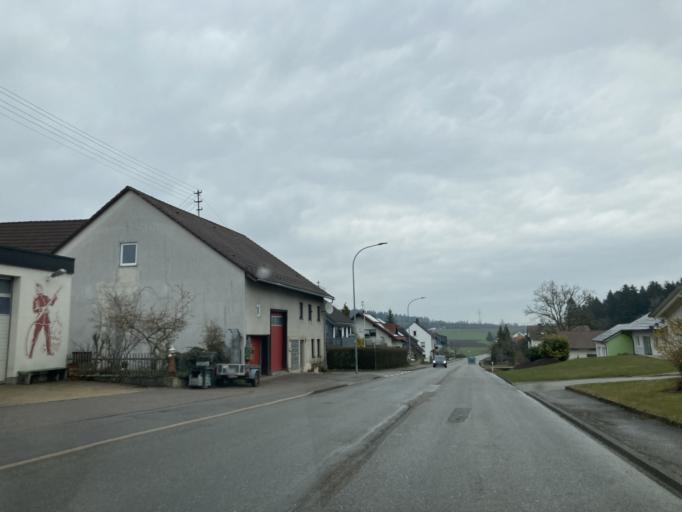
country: DE
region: Baden-Wuerttemberg
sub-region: Freiburg Region
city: Aichhalden
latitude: 48.2560
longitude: 8.4491
